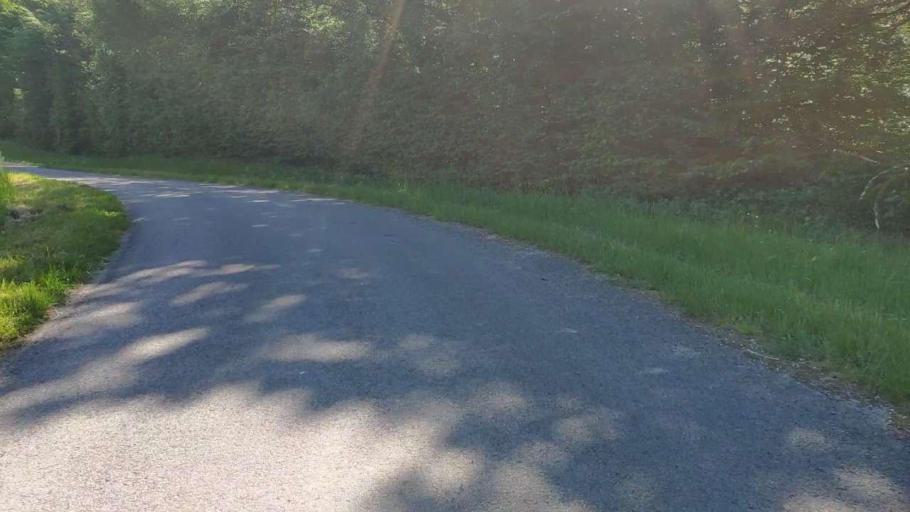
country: FR
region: Franche-Comte
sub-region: Departement du Jura
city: Bletterans
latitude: 46.7986
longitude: 5.4405
